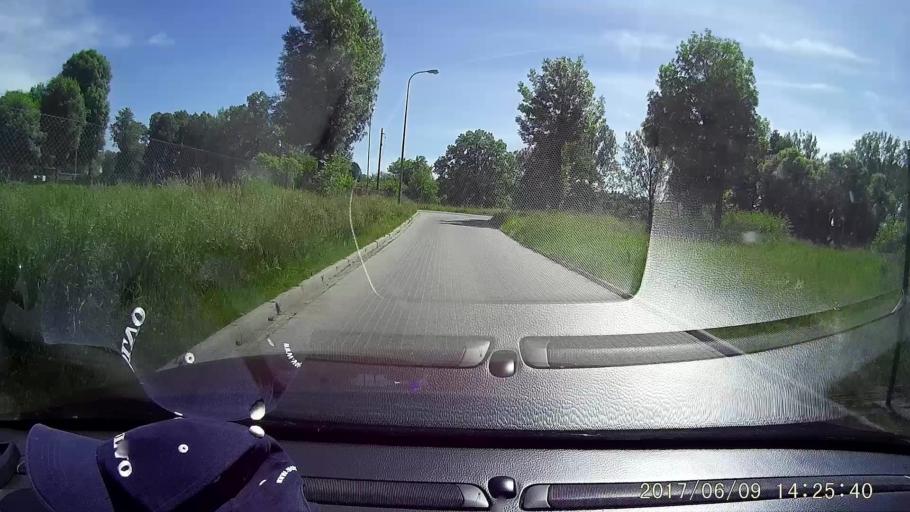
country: PL
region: Lower Silesian Voivodeship
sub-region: Powiat zgorzelecki
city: Zgorzelec
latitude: 51.1338
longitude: 15.0171
